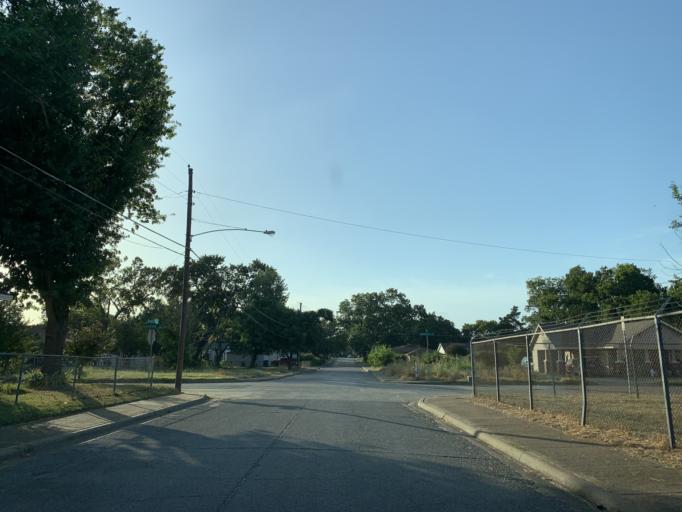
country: US
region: Texas
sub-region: Dallas County
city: Dallas
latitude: 32.7584
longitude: -96.7452
